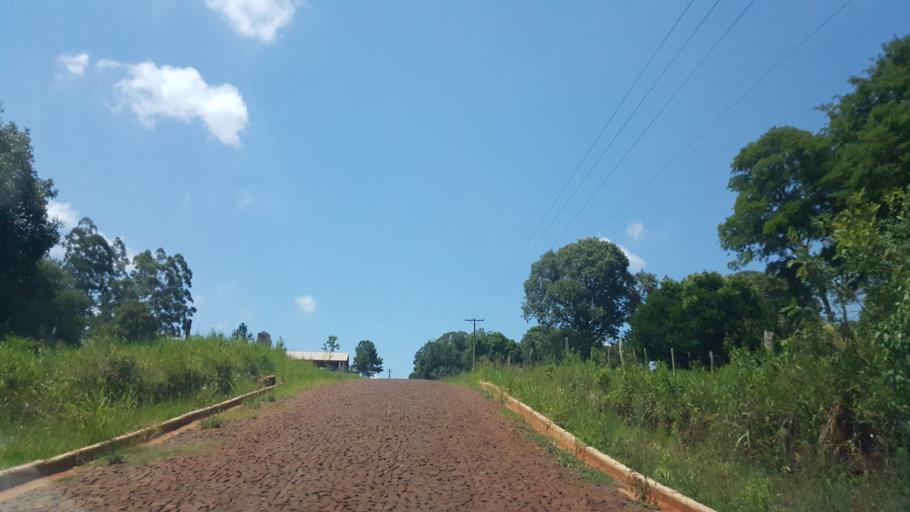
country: AR
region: Misiones
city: Capiovi
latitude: -26.9227
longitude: -55.0521
